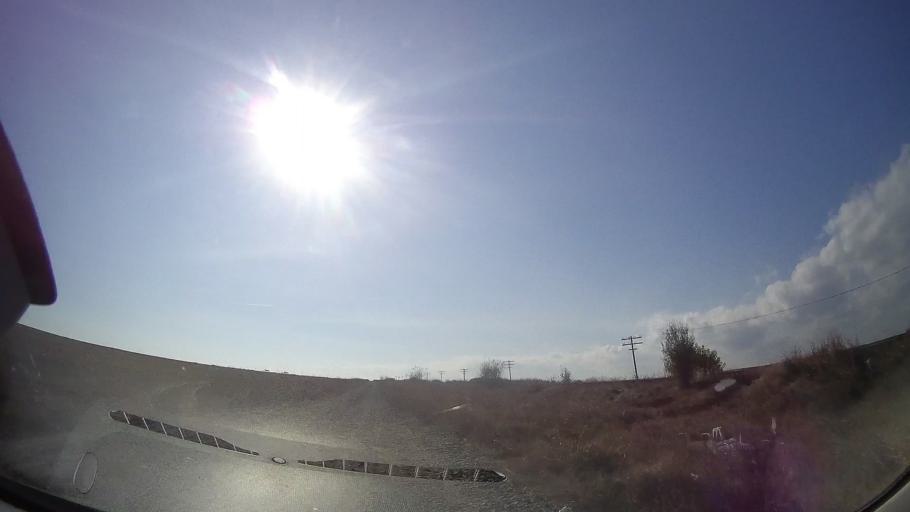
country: RO
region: Constanta
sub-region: Comuna Costinesti
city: Schitu
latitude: 43.9221
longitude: 28.6312
